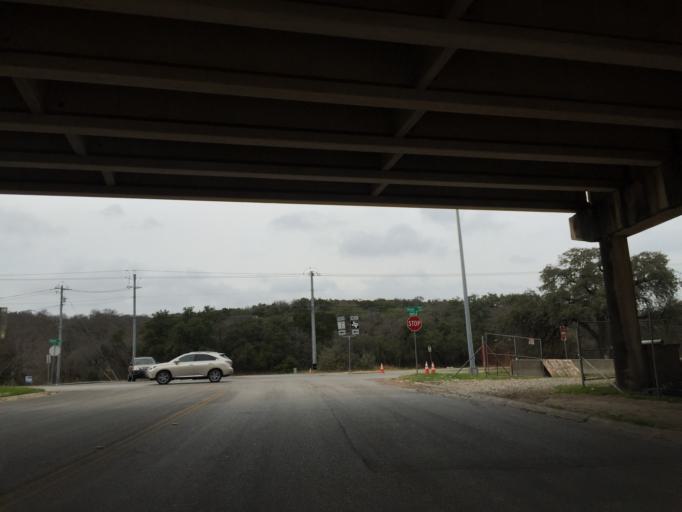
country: US
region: Texas
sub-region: Travis County
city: Rollingwood
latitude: 30.2687
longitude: -97.7774
